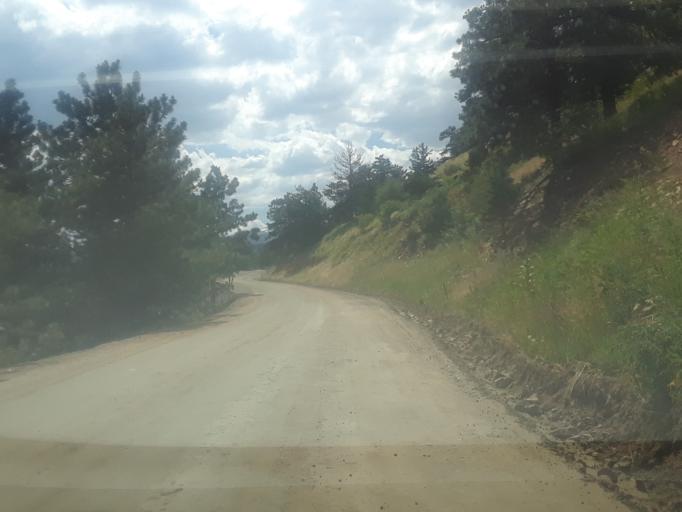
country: US
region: Colorado
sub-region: Boulder County
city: Nederland
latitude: 40.0485
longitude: -105.4651
